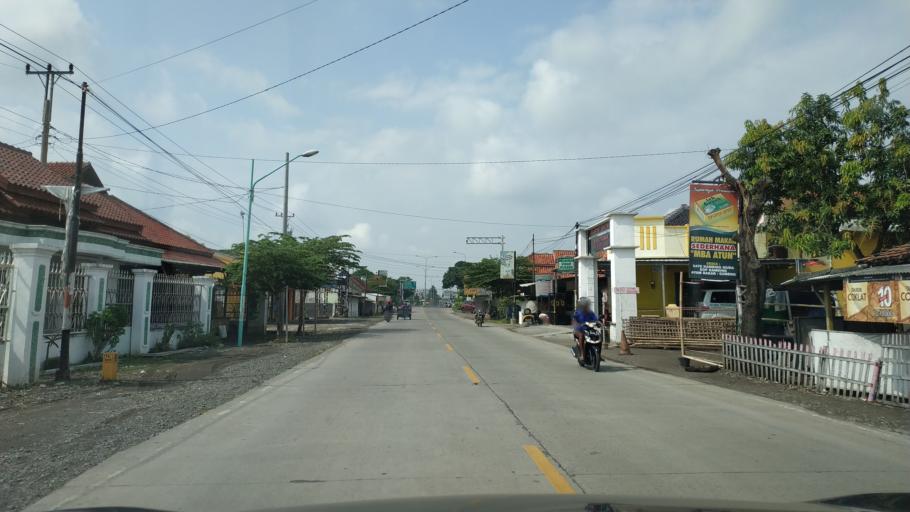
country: ID
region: Central Java
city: Ketanggungan
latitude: -6.8925
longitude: 108.8856
